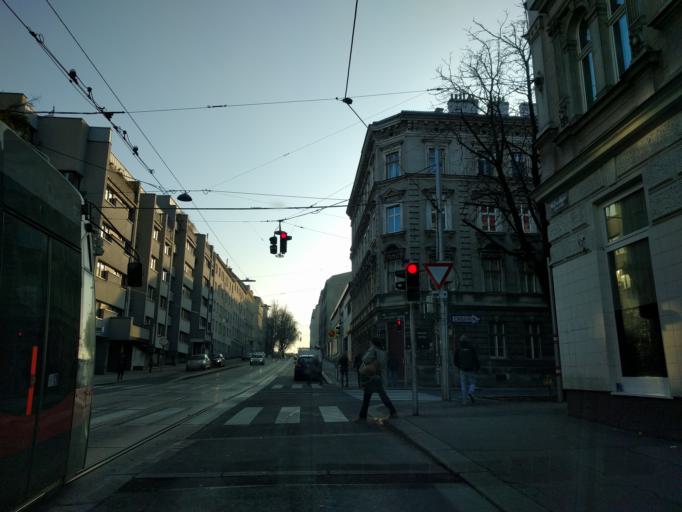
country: AT
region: Vienna
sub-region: Wien Stadt
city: Vienna
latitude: 48.2082
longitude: 16.3244
